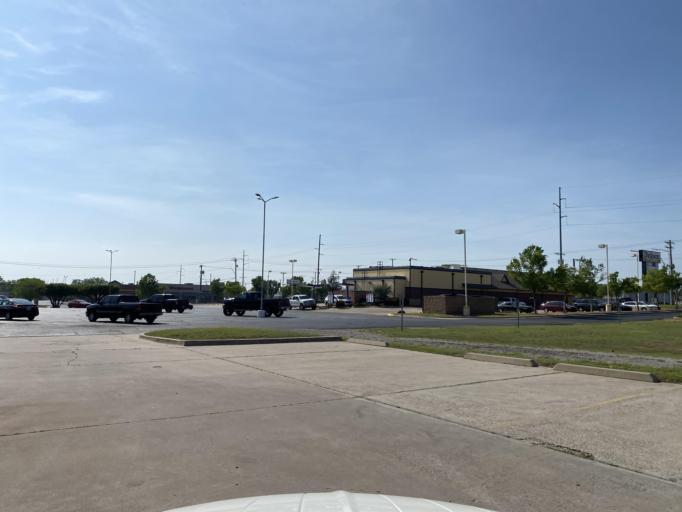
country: US
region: Oklahoma
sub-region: Oklahoma County
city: Midwest City
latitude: 35.4486
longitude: -97.3517
